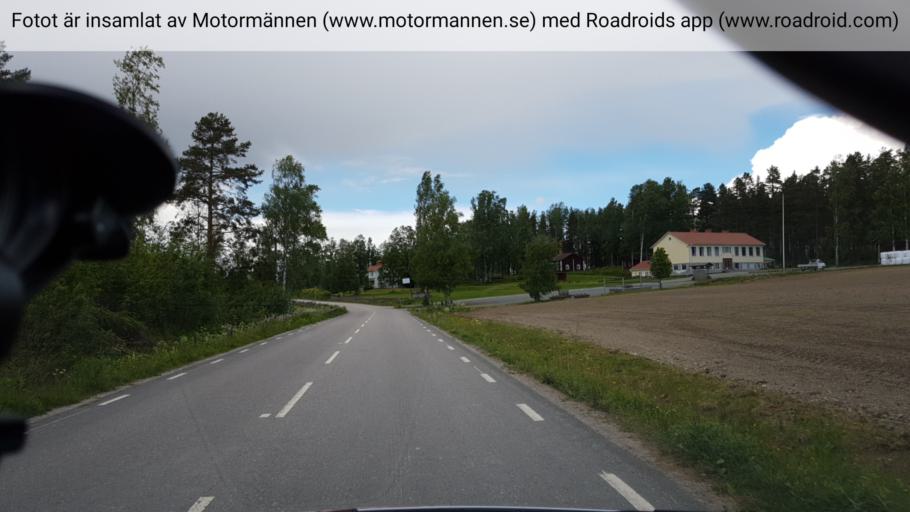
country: SE
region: Gaevleborg
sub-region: Ovanakers Kommun
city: Alfta
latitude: 61.2422
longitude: 16.1467
